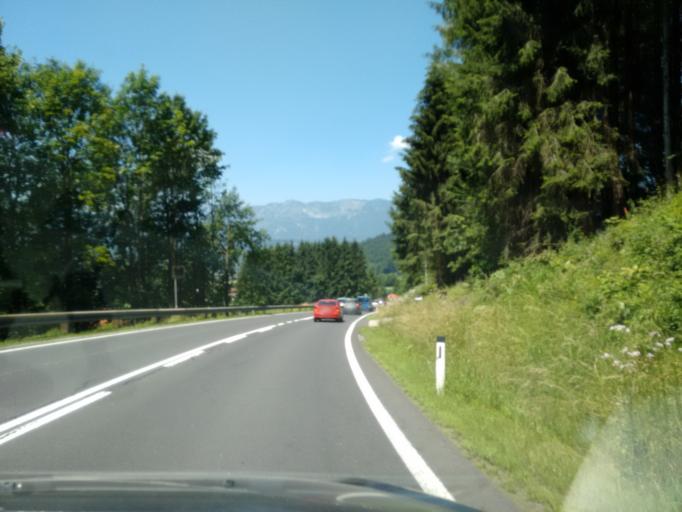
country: AT
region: Upper Austria
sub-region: Politischer Bezirk Gmunden
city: Bad Goisern
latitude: 47.6174
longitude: 13.6540
